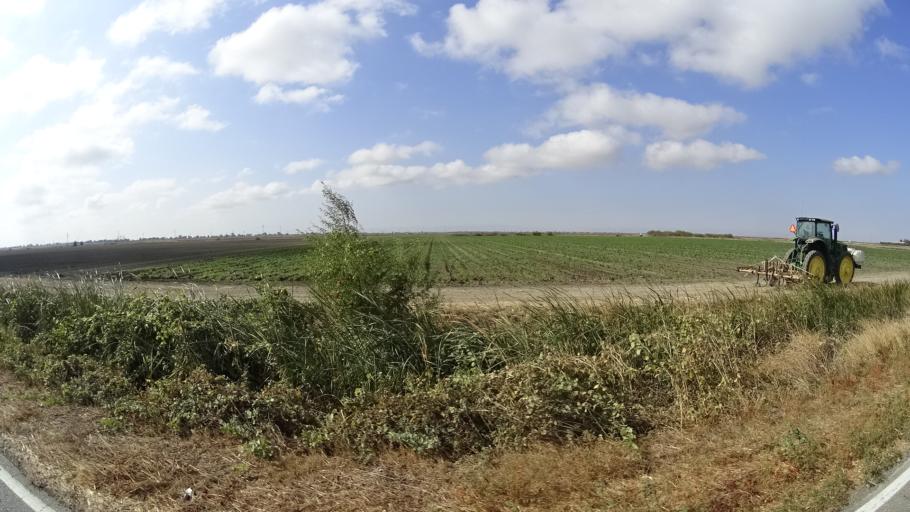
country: US
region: California
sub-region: Yolo County
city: Woodland
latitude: 38.8192
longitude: -121.7416
